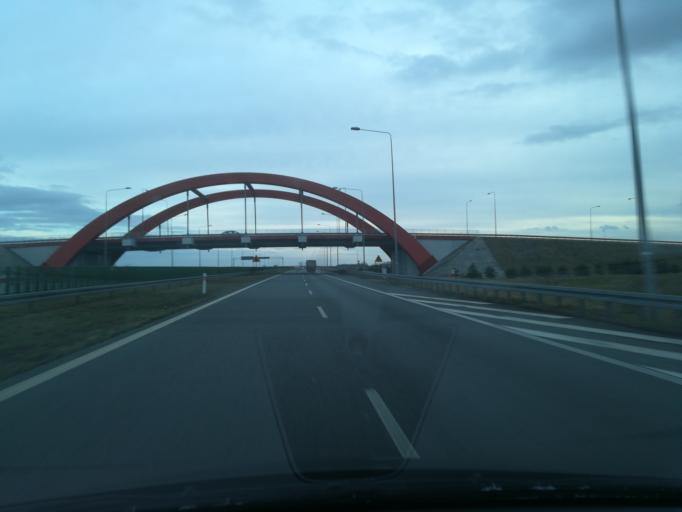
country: PL
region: Lodz Voivodeship
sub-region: Powiat leczycki
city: Piatek
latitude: 52.0652
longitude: 19.5354
